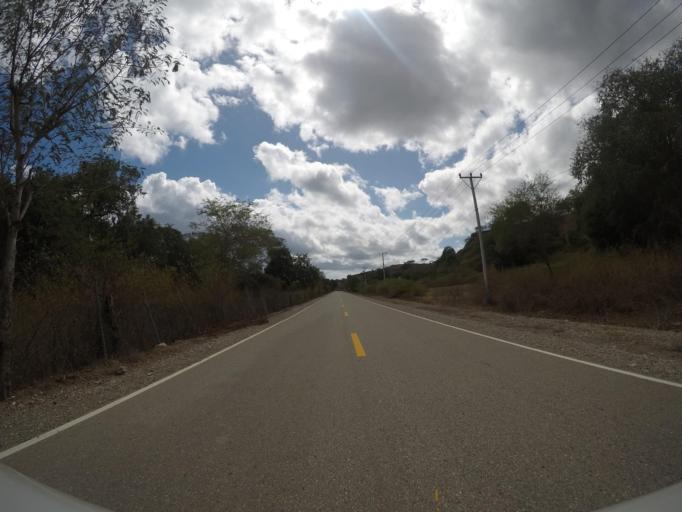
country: TL
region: Lautem
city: Lospalos
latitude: -8.4079
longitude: 126.8114
